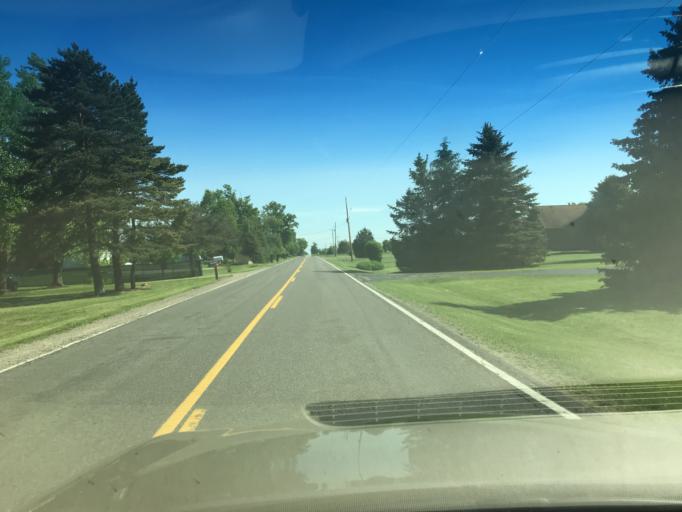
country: US
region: Michigan
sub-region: Ingham County
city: Mason
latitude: 42.5380
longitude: -84.4625
